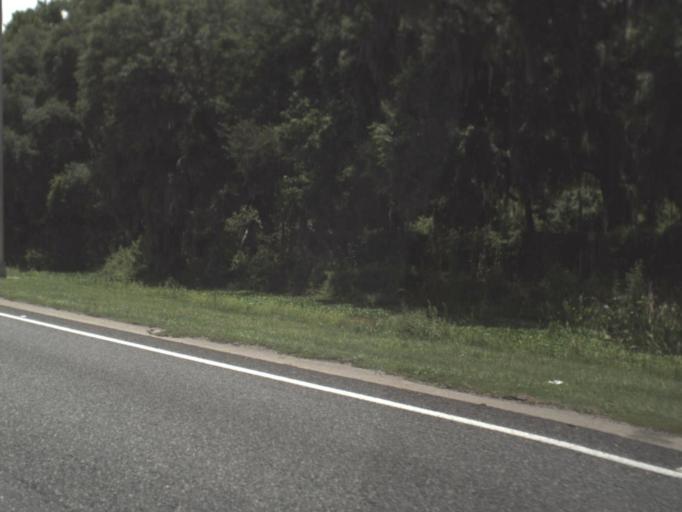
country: US
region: Florida
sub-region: Alachua County
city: Gainesville
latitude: 29.5924
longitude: -82.3649
